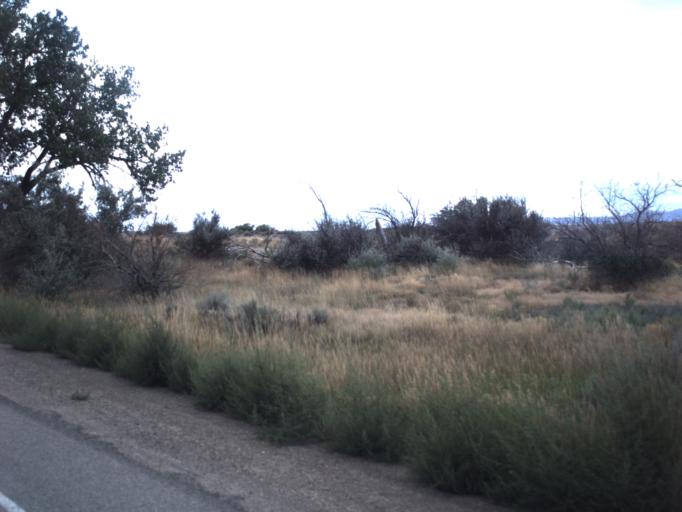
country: US
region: Utah
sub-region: Carbon County
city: Price
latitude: 39.5747
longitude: -110.8161
